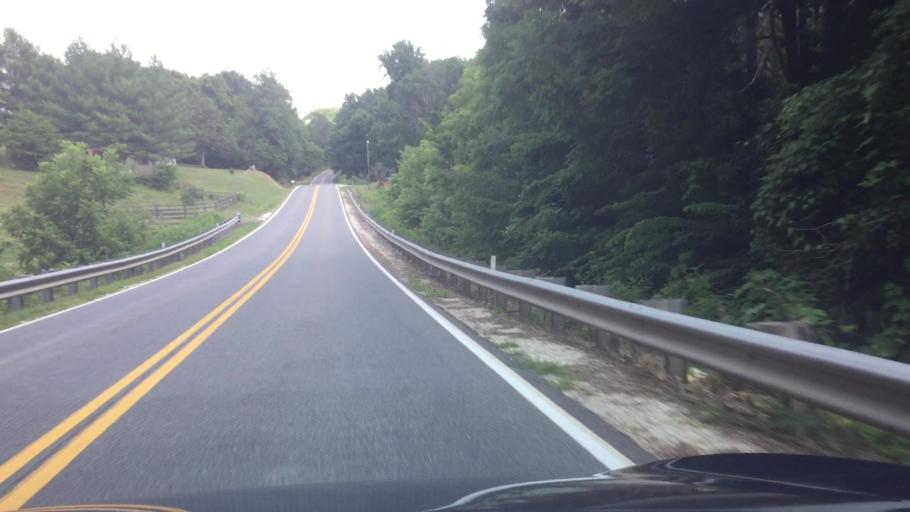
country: US
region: Virginia
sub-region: Appomattox County
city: Appomattox
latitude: 37.3411
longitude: -78.8923
